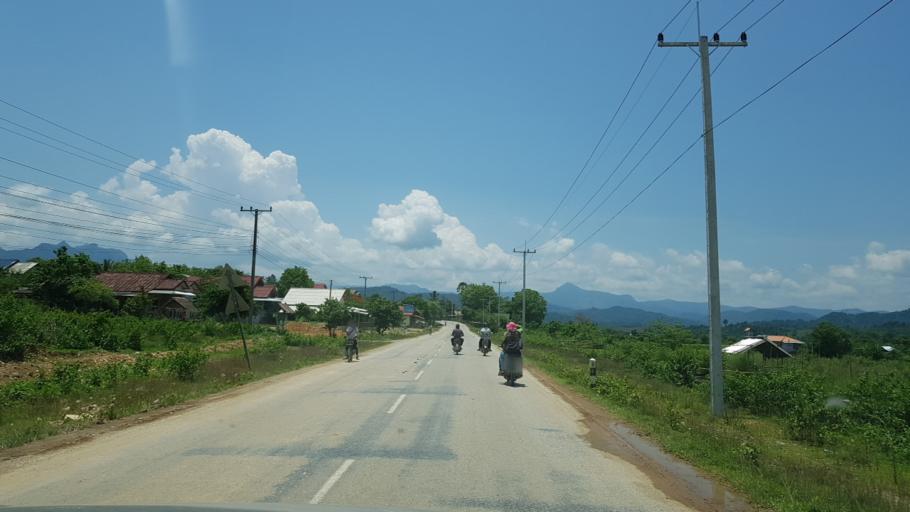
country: LA
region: Vientiane
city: Muang Kasi
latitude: 19.2564
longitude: 102.2338
